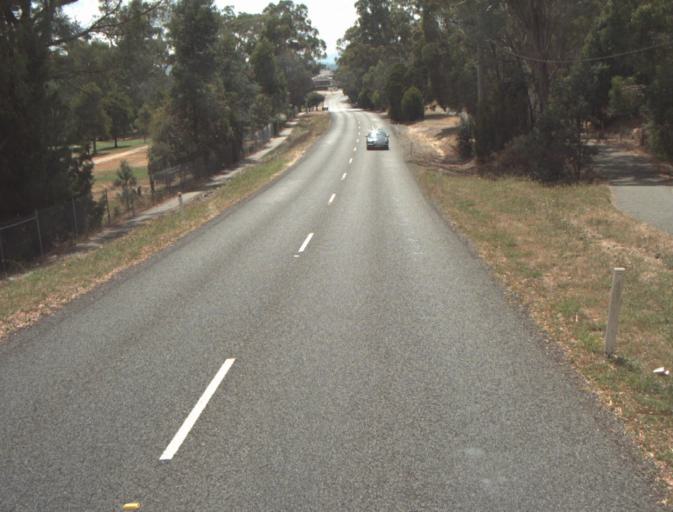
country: AU
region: Tasmania
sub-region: Launceston
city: Newstead
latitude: -41.4657
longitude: 147.1692
